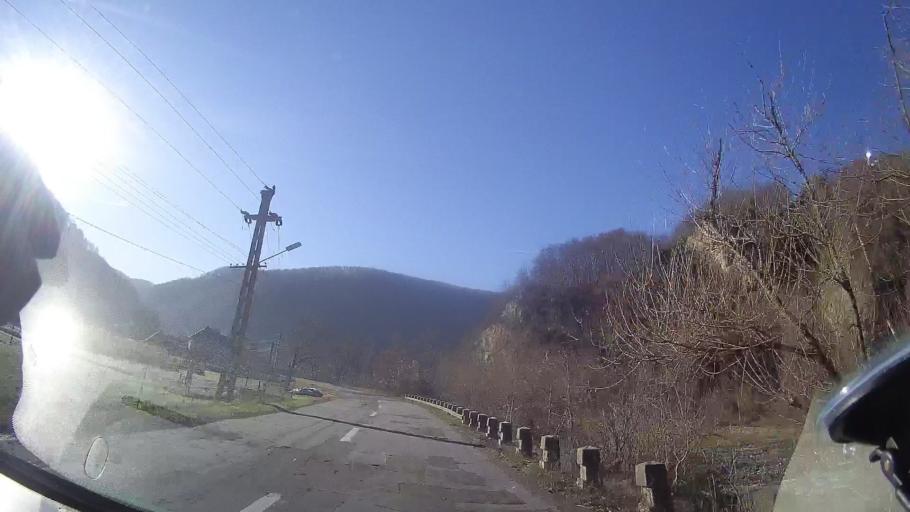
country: RO
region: Bihor
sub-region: Comuna Bulz
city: Bulz
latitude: 46.9275
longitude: 22.6575
